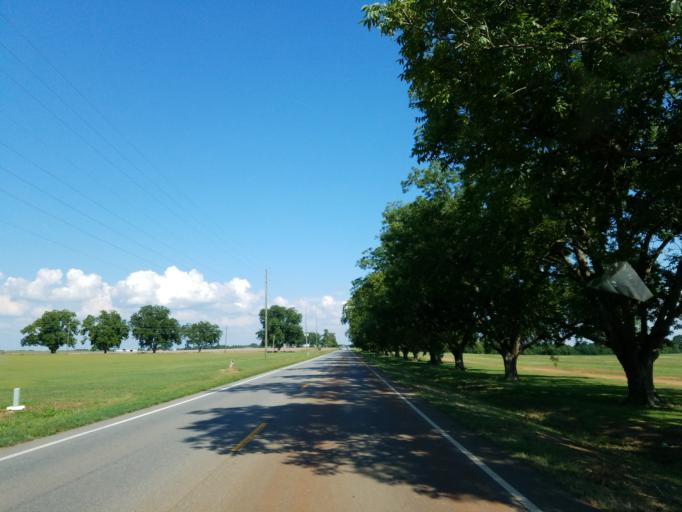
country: US
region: Georgia
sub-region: Peach County
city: Fort Valley
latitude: 32.5835
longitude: -83.9225
